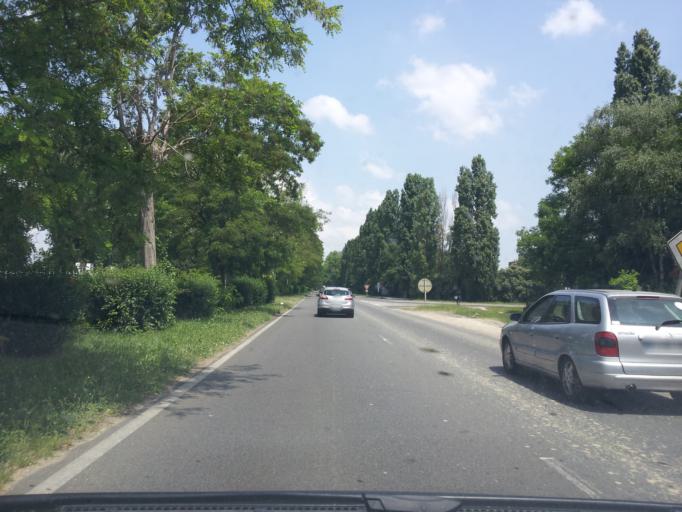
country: FR
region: Ile-de-France
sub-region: Departement de l'Essonne
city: Fleury-Merogis
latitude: 48.6423
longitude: 2.3635
